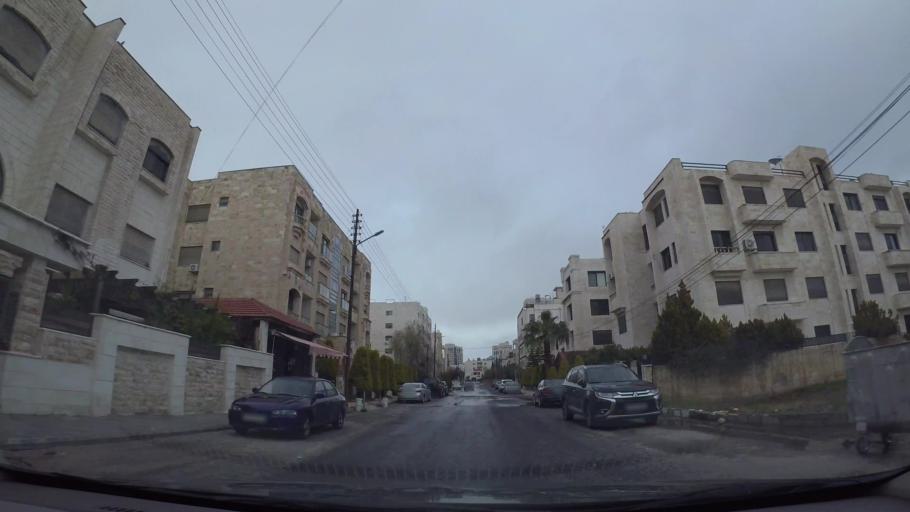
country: JO
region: Amman
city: Wadi as Sir
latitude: 31.9514
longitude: 35.8752
